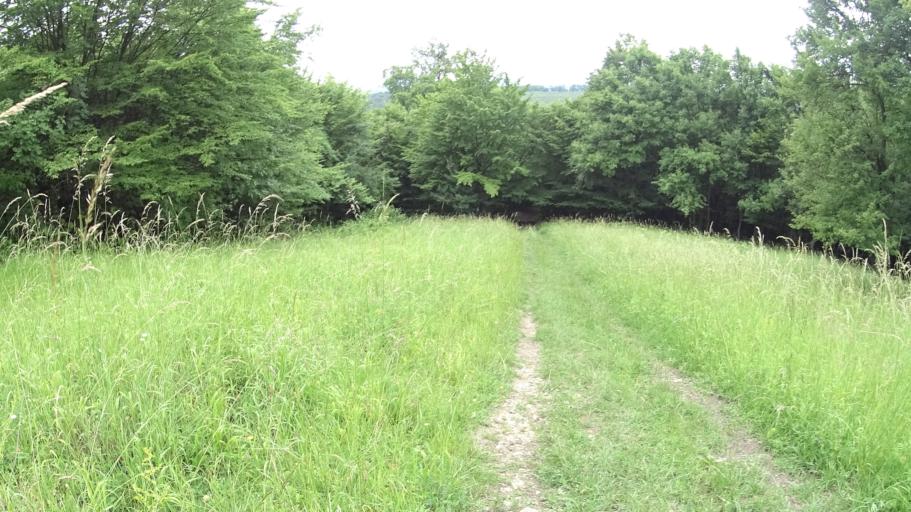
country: HU
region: Pest
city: Nagymaros
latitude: 47.8132
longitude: 18.9354
